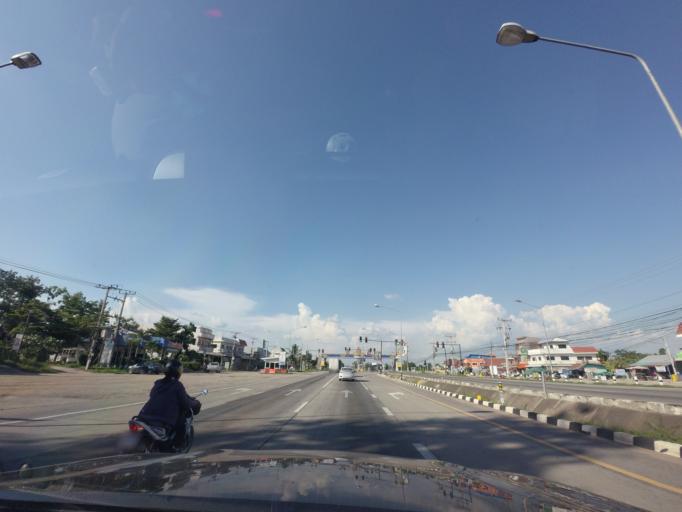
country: TH
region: Khon Kaen
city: Non Sila
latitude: 15.9656
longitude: 102.6911
